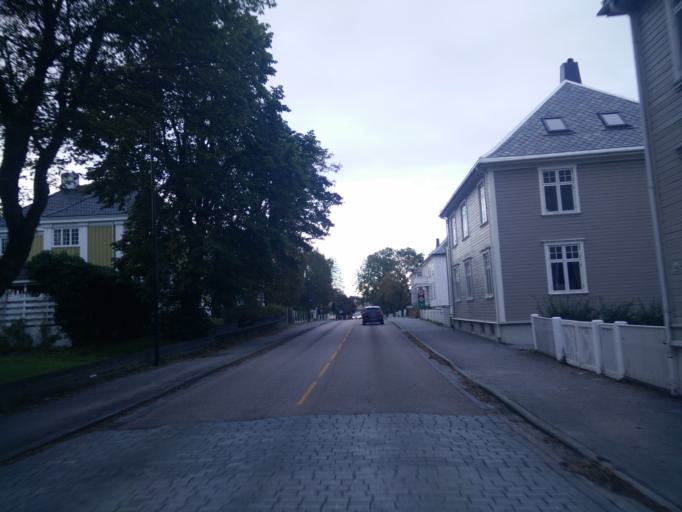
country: NO
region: More og Romsdal
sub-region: Kristiansund
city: Kristiansund
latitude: 63.1165
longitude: 7.7246
